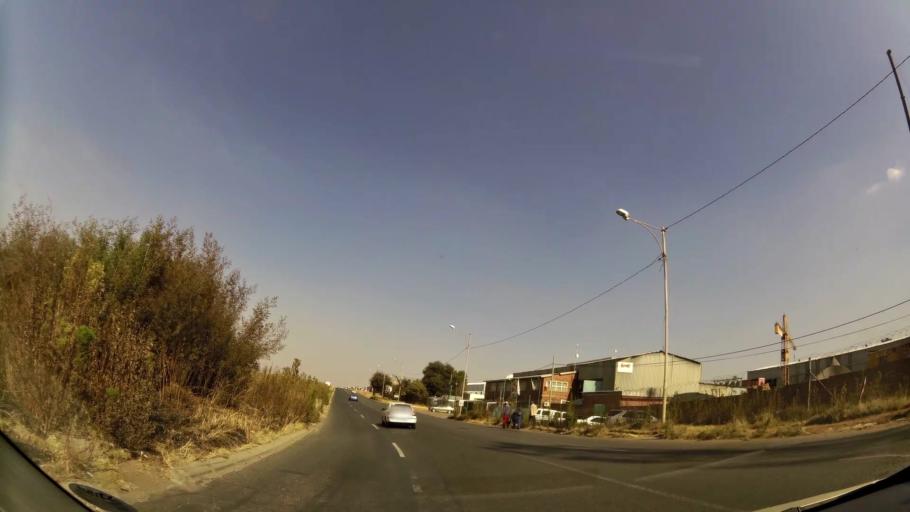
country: ZA
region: Gauteng
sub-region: City of Johannesburg Metropolitan Municipality
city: Roodepoort
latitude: -26.1583
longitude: 27.8049
